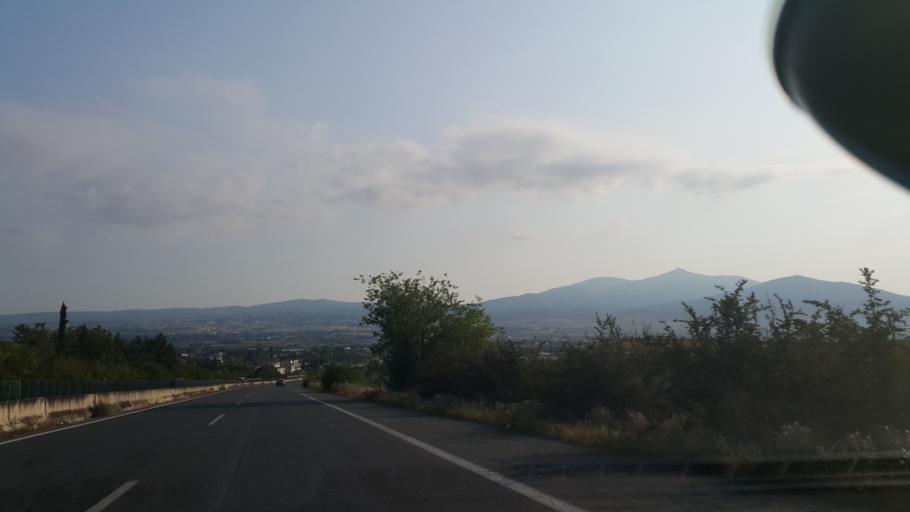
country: GR
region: Central Macedonia
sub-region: Nomos Thessalonikis
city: Neo Rysi
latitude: 40.4891
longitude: 22.9983
